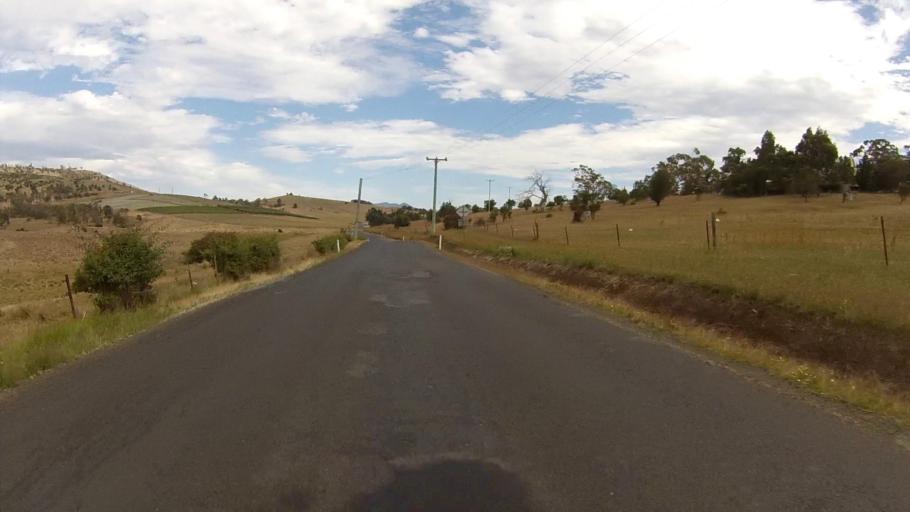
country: AU
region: Tasmania
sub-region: Brighton
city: Old Beach
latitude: -42.7123
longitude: 147.3207
